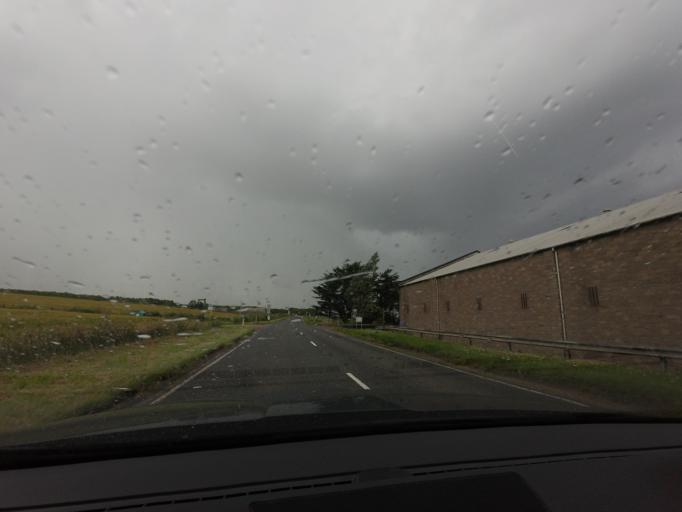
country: GB
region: Scotland
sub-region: Moray
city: Buckie
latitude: 57.6613
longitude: -2.9625
